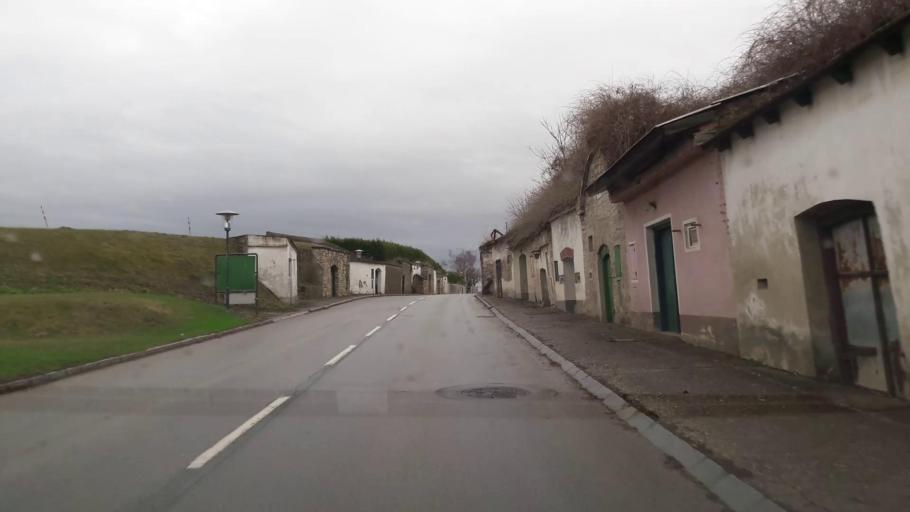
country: AT
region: Lower Austria
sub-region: Politischer Bezirk Bruck an der Leitha
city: Scharndorf
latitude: 48.0632
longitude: 16.7921
